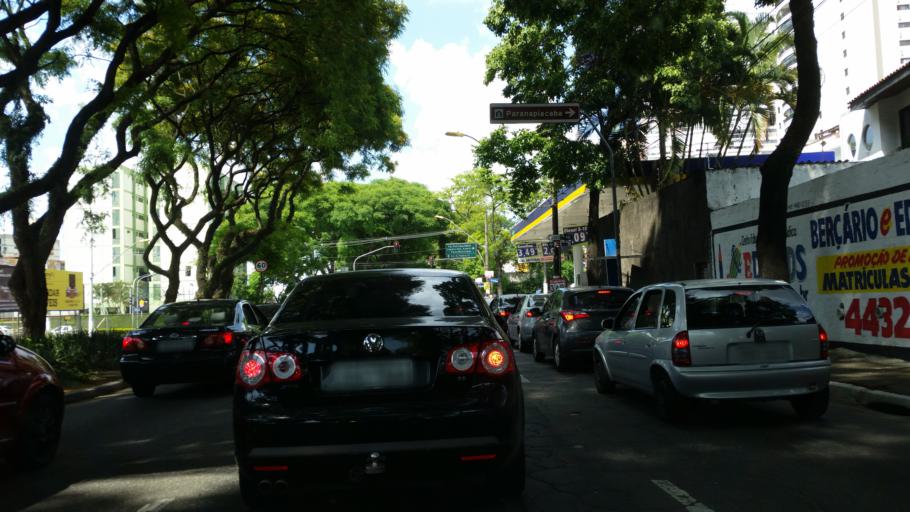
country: BR
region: Sao Paulo
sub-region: Santo Andre
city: Santo Andre
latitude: -23.6457
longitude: -46.5427
